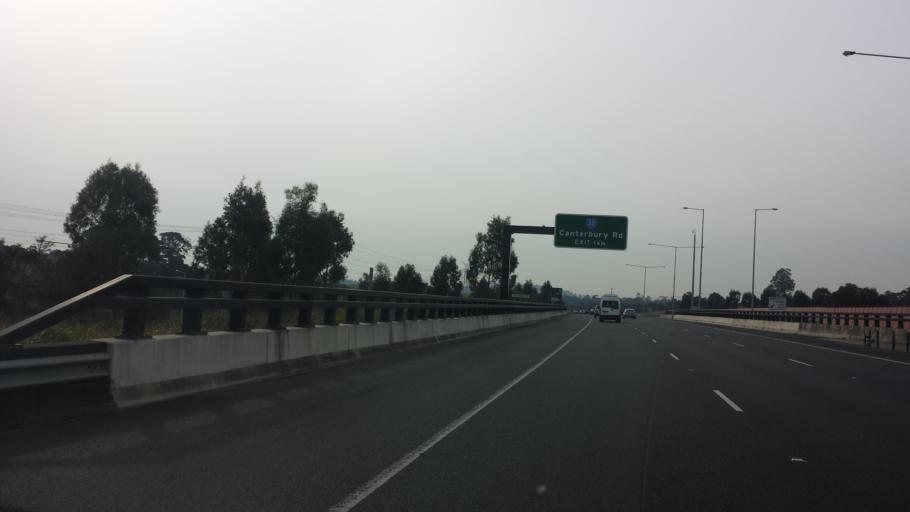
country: AU
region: Victoria
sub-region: Knox
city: Wantirna
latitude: -37.8473
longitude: 145.2166
